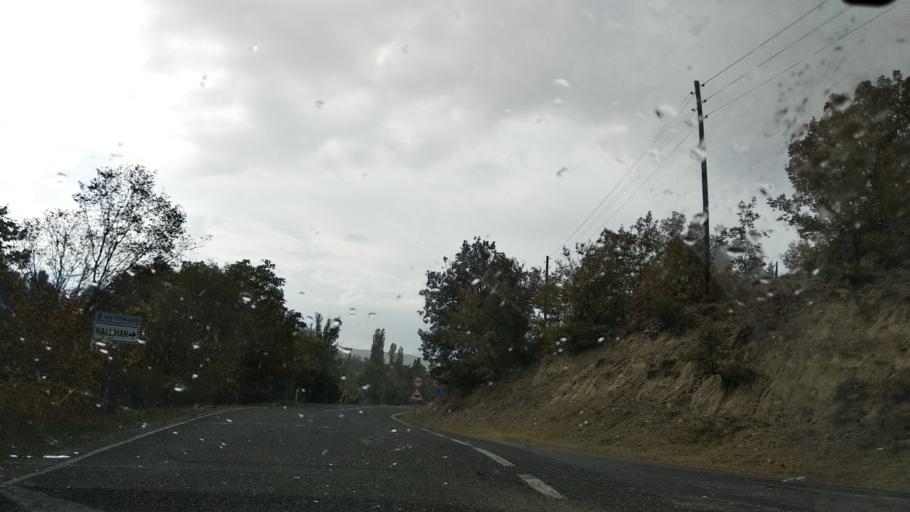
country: TR
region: Ankara
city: Nallihan
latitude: 40.3342
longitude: 31.4150
